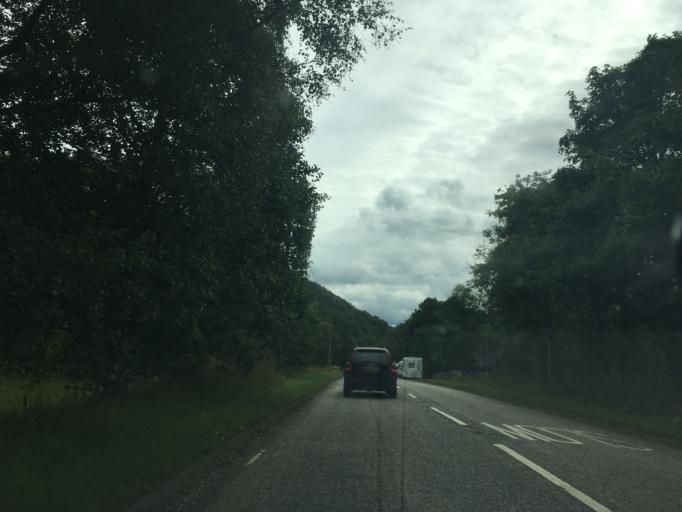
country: GB
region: Scotland
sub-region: Stirling
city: Callander
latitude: 56.2590
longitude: -4.2847
